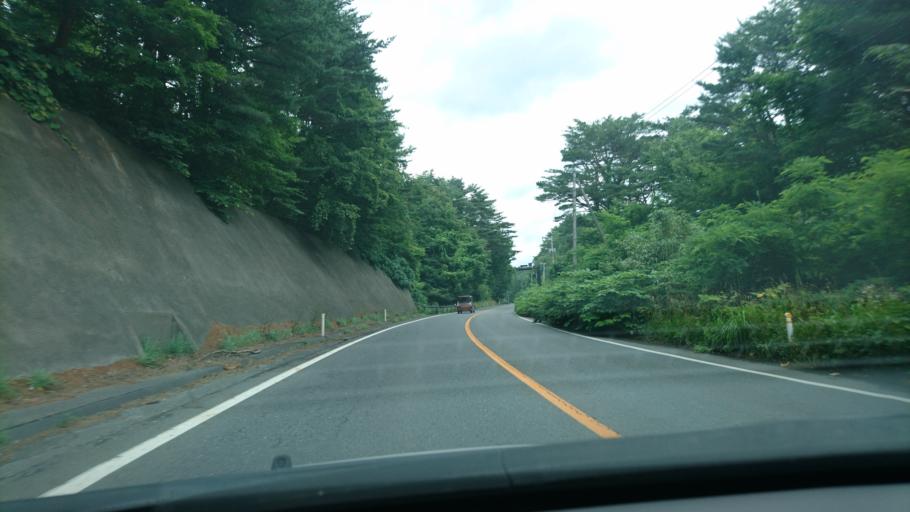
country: JP
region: Iwate
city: Otsuchi
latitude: 39.3904
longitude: 141.9427
